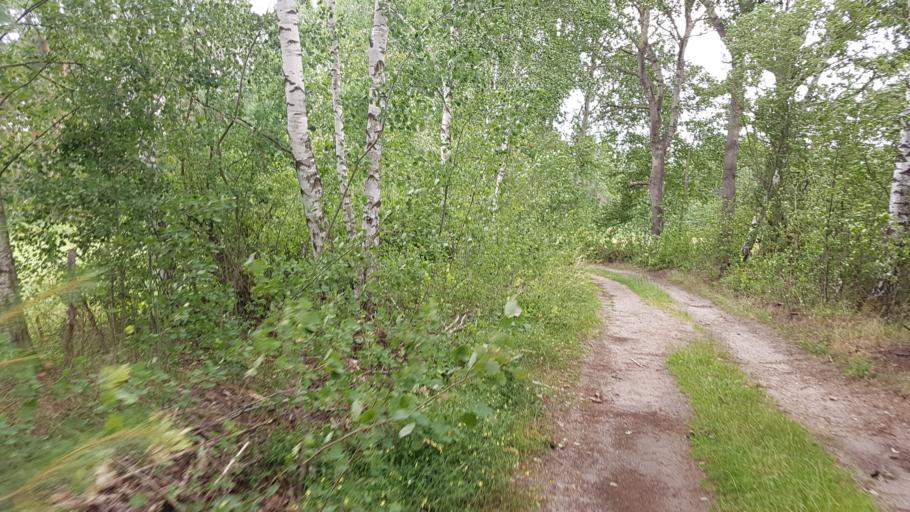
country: DE
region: Brandenburg
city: Doberlug-Kirchhain
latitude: 51.6349
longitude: 13.5993
